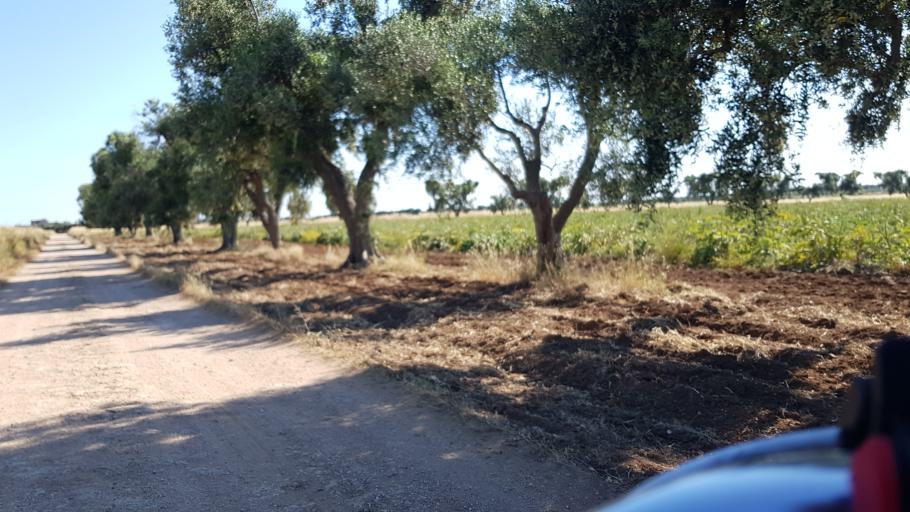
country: IT
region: Apulia
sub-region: Provincia di Brindisi
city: Mesagne
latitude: 40.6235
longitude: 17.8526
